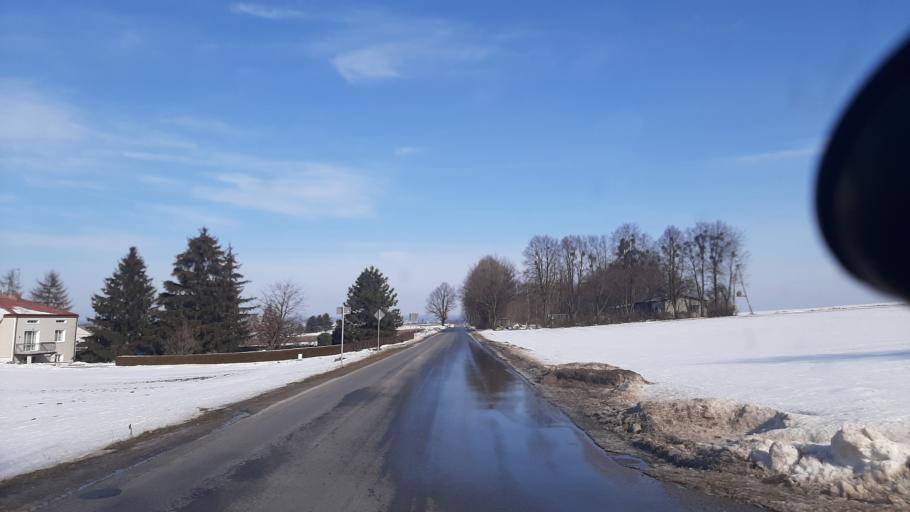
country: PL
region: Lublin Voivodeship
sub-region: Powiat pulawski
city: Kurow
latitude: 51.3617
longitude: 22.1384
